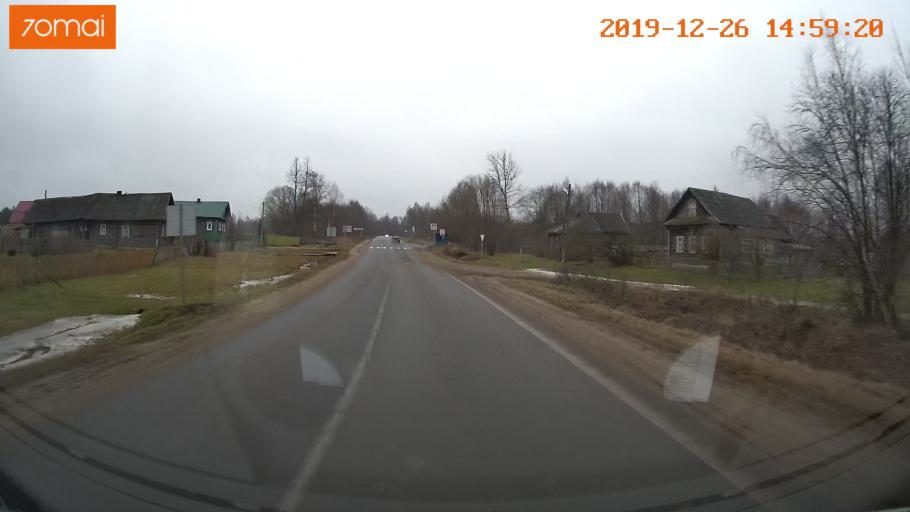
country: RU
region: Jaroslavl
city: Rybinsk
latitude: 58.2599
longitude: 38.8473
